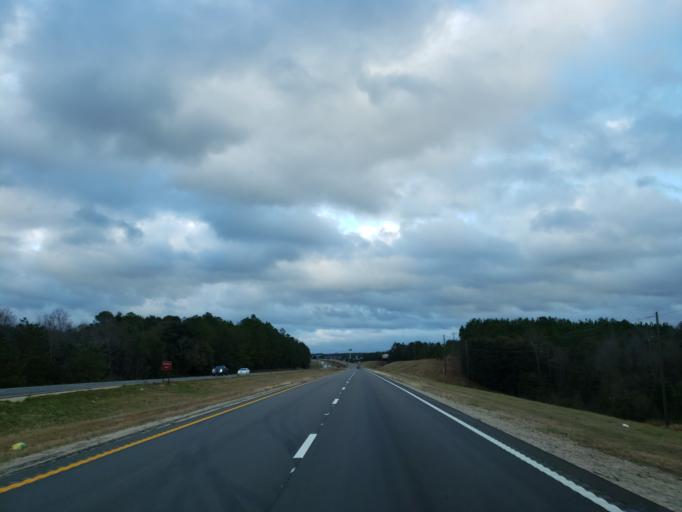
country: US
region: Mississippi
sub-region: George County
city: Lucedale
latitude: 30.9544
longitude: -88.6088
